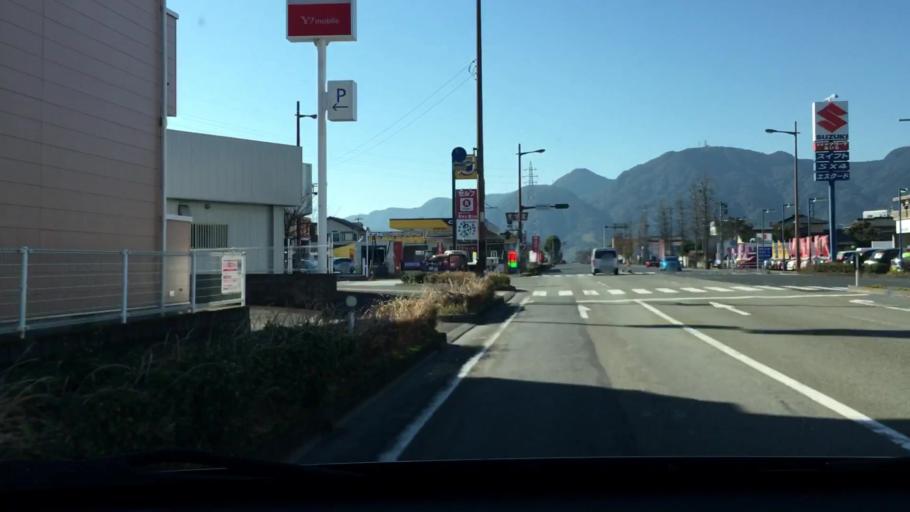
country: JP
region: Kagoshima
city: Kajiki
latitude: 31.7264
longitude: 130.6243
